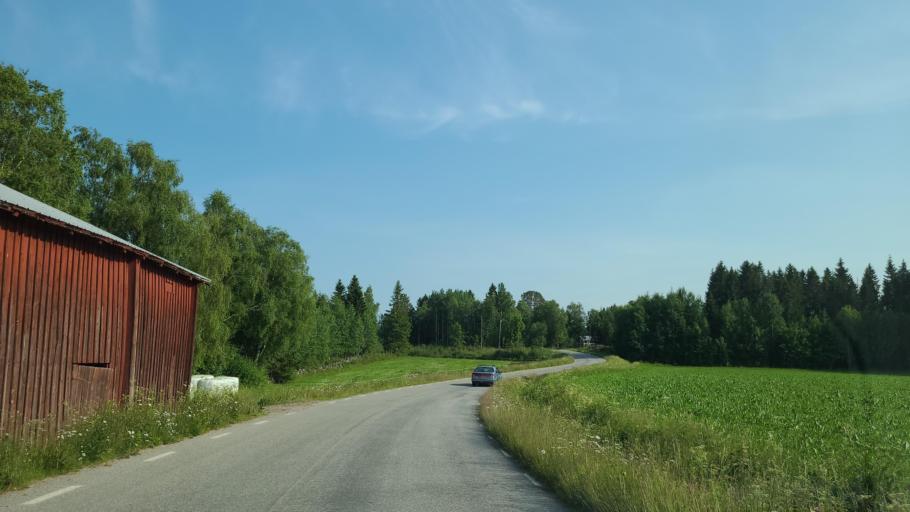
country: SE
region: Vaesterbotten
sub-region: Skelleftea Kommun
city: Burea
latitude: 64.3470
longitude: 21.3395
